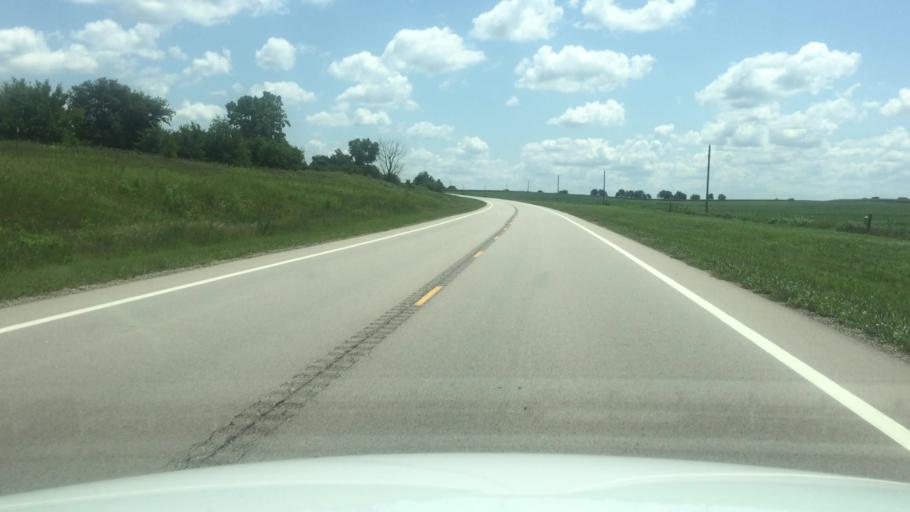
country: US
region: Kansas
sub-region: Brown County
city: Horton
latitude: 39.6160
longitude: -95.3479
